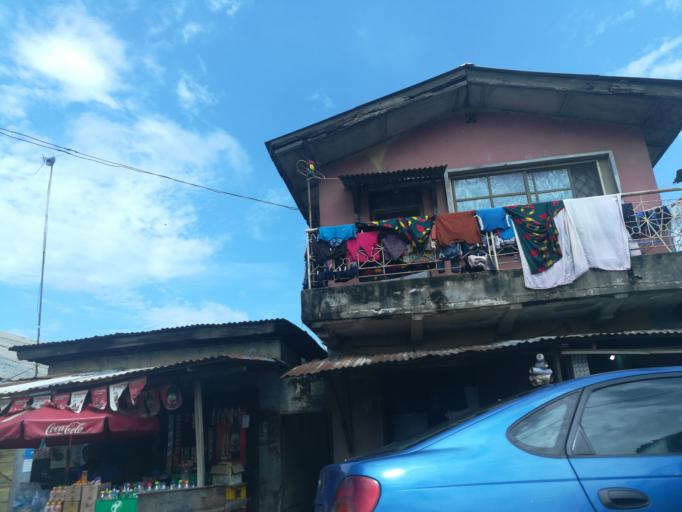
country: NG
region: Lagos
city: Agege
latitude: 6.6218
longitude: 3.3315
